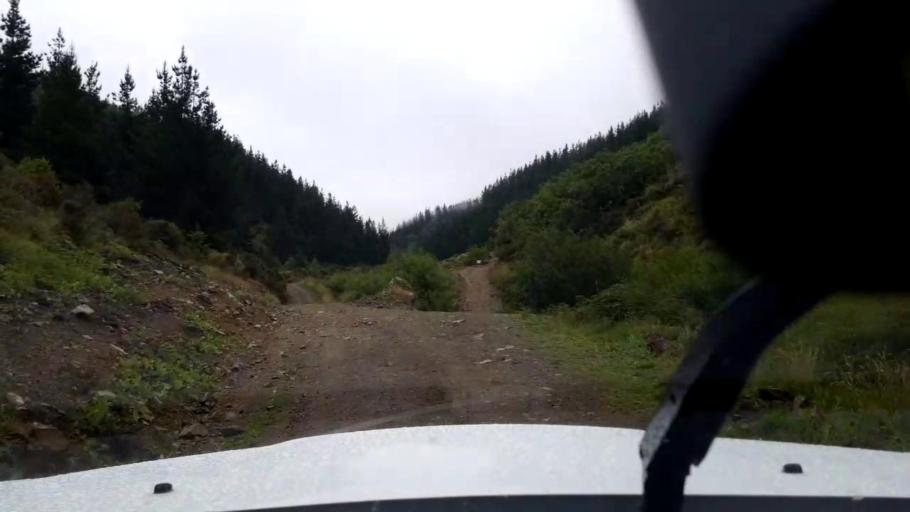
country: NZ
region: Canterbury
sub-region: Timaru District
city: Pleasant Point
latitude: -44.0338
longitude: 170.9924
